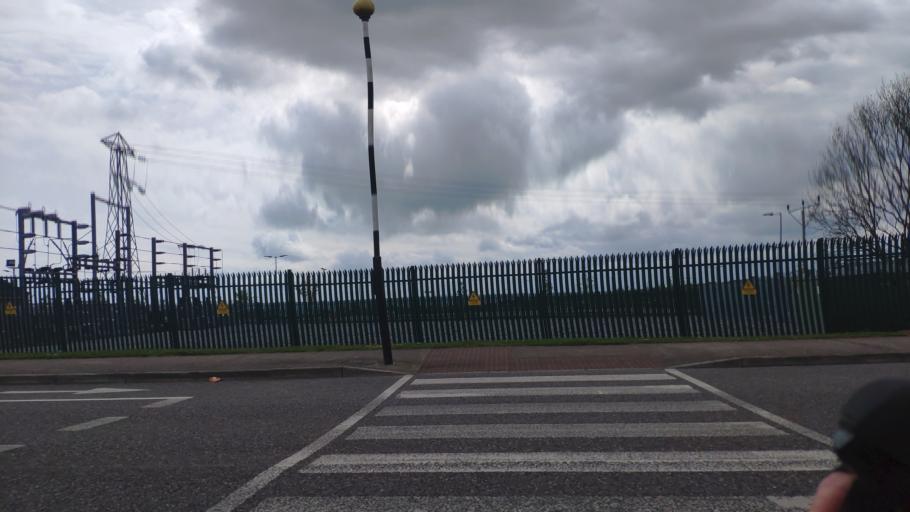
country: IE
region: Munster
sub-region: County Cork
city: Cork
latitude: 51.9080
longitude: -8.5122
